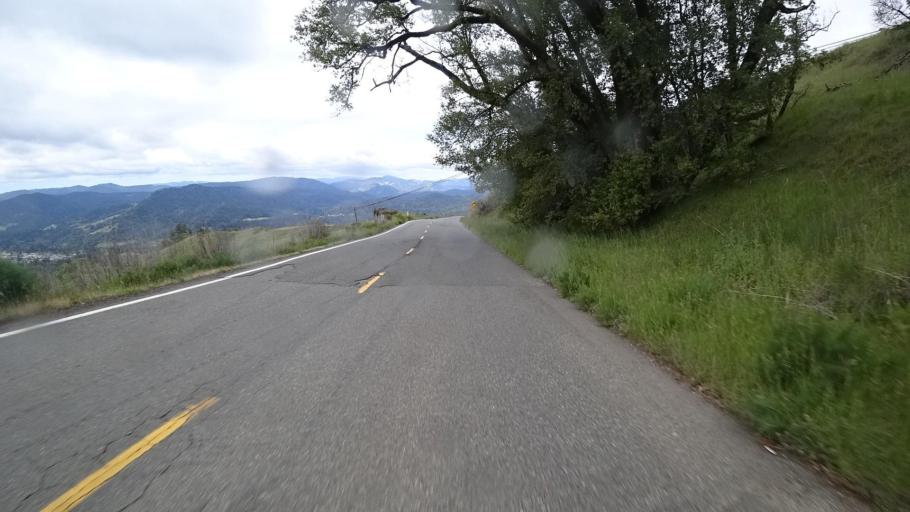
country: US
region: California
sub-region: Humboldt County
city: Redway
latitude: 40.1121
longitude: -123.7713
